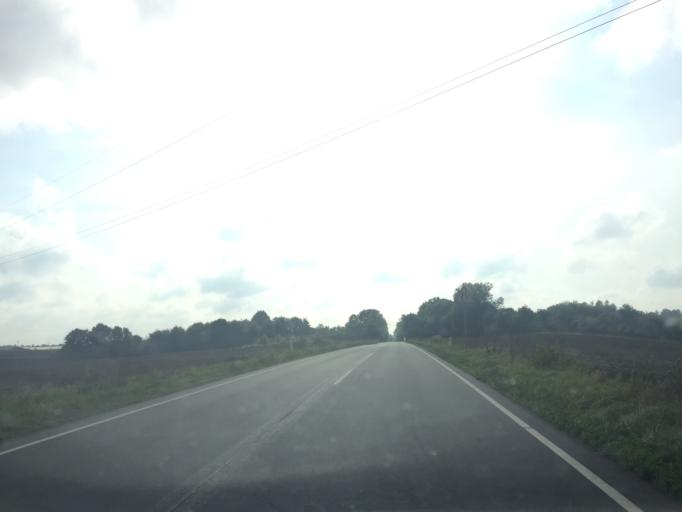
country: DK
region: Zealand
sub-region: Holbaek Kommune
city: Tollose
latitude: 55.6182
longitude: 11.7873
